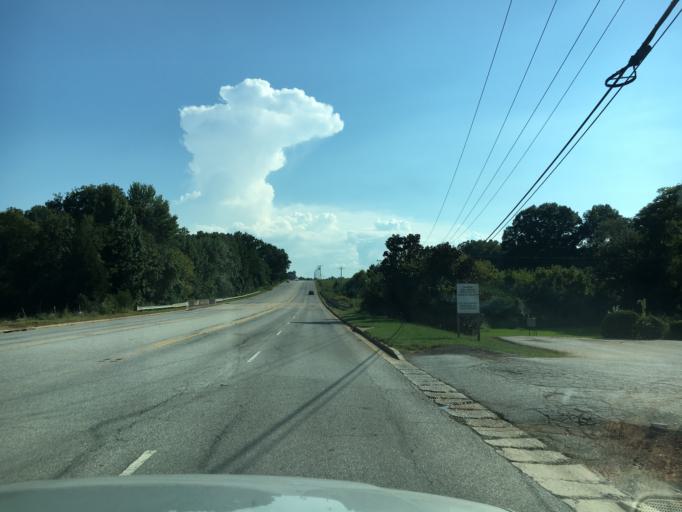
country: US
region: South Carolina
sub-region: Laurens County
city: Clinton
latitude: 34.4440
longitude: -81.8890
